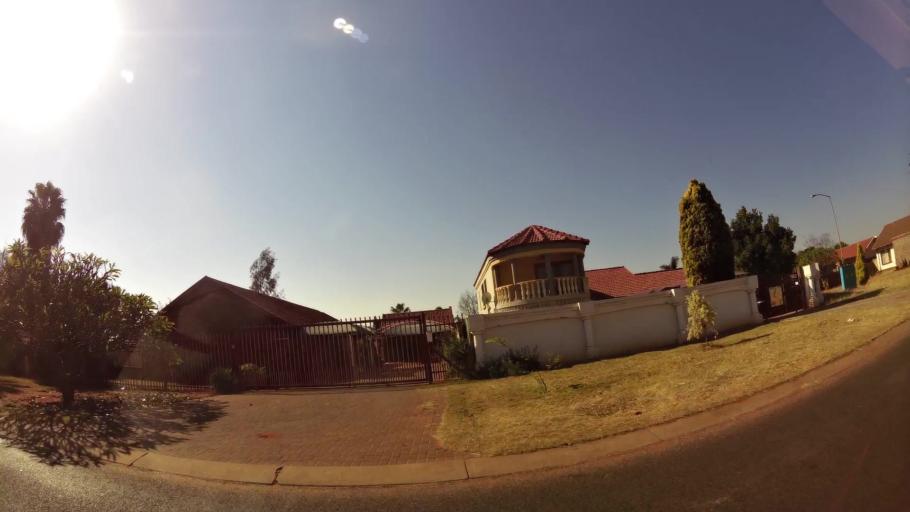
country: ZA
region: North-West
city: Ga-Rankuwa
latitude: -25.6486
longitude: 28.1094
